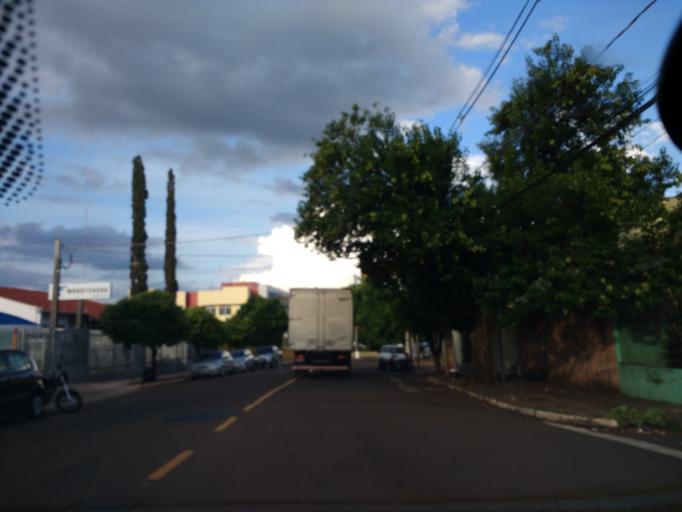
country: BR
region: Parana
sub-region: Londrina
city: Londrina
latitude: -23.2950
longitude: -51.1701
